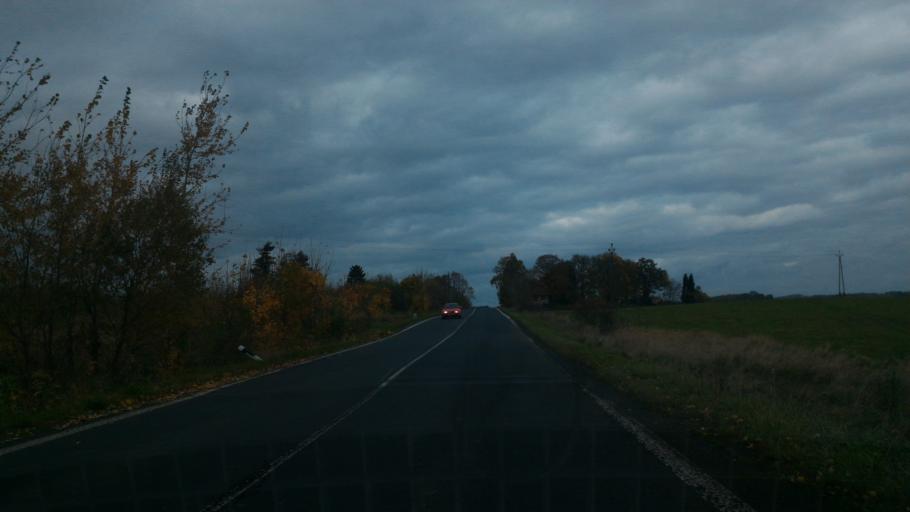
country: CZ
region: Ustecky
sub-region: Okres Decin
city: Rumburk
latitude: 50.9389
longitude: 14.5582
